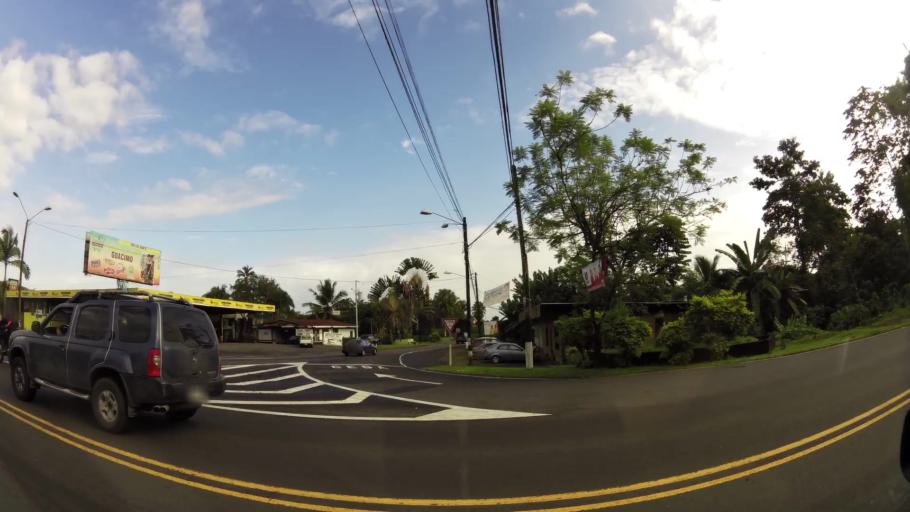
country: CR
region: Limon
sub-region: Canton de Guacimo
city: Guacimo
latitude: 10.2059
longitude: -83.6847
